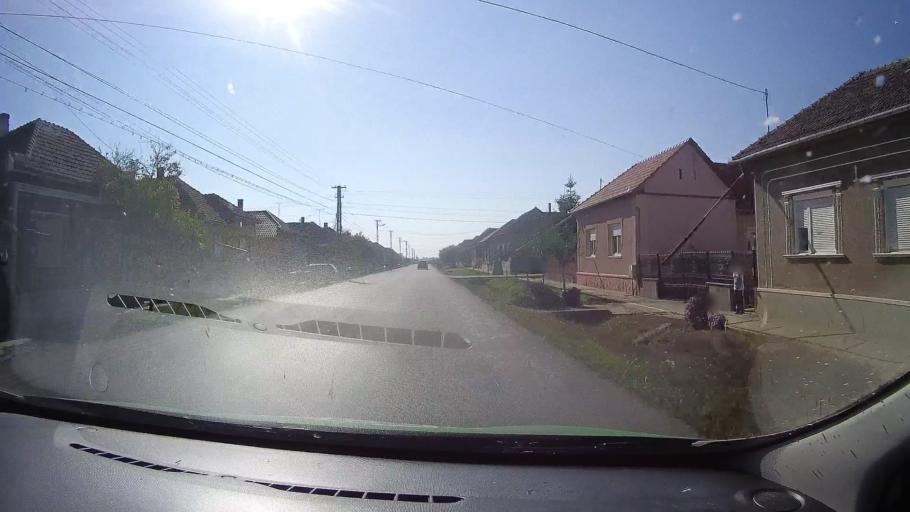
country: RO
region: Satu Mare
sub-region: Comuna Camin
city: Camin
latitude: 47.7253
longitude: 22.4762
